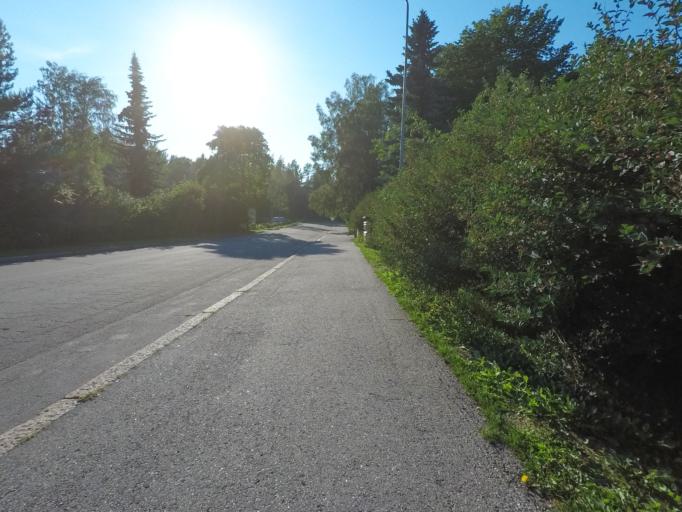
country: FI
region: Uusimaa
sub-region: Helsinki
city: Vantaa
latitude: 60.2244
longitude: 25.0921
